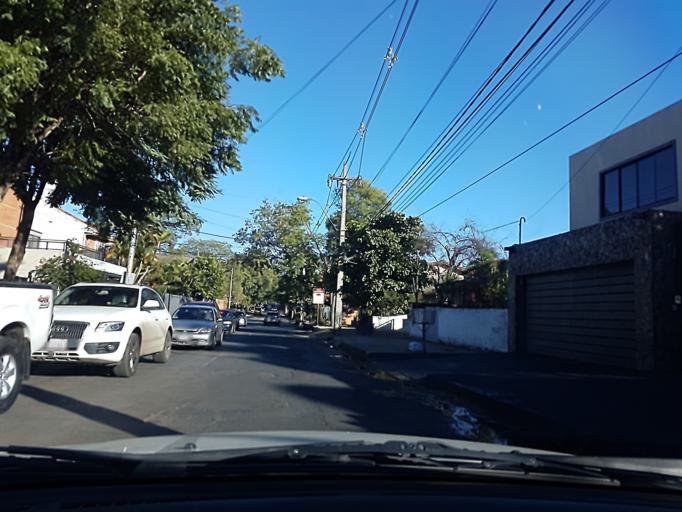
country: PY
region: Asuncion
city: Asuncion
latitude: -25.2799
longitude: -57.5799
